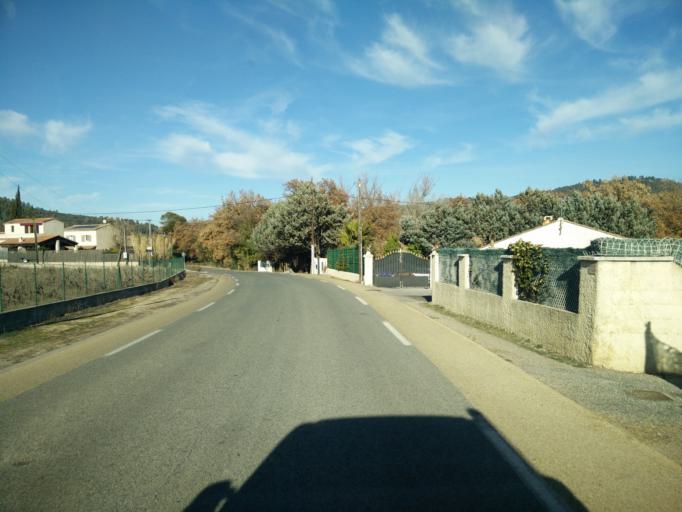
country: FR
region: Provence-Alpes-Cote d'Azur
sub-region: Departement du Var
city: Taradeau
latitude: 43.4427
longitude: 6.4237
